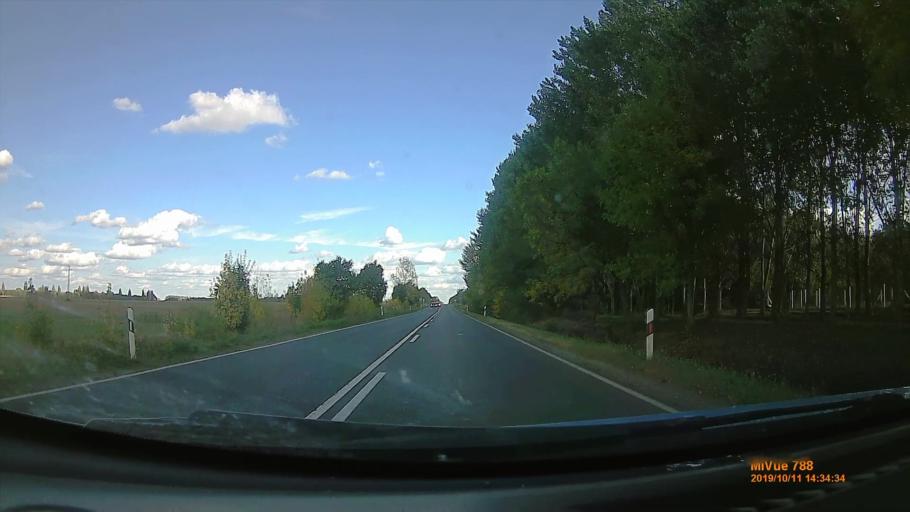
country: HU
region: Hajdu-Bihar
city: Ebes
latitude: 47.5604
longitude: 21.4771
